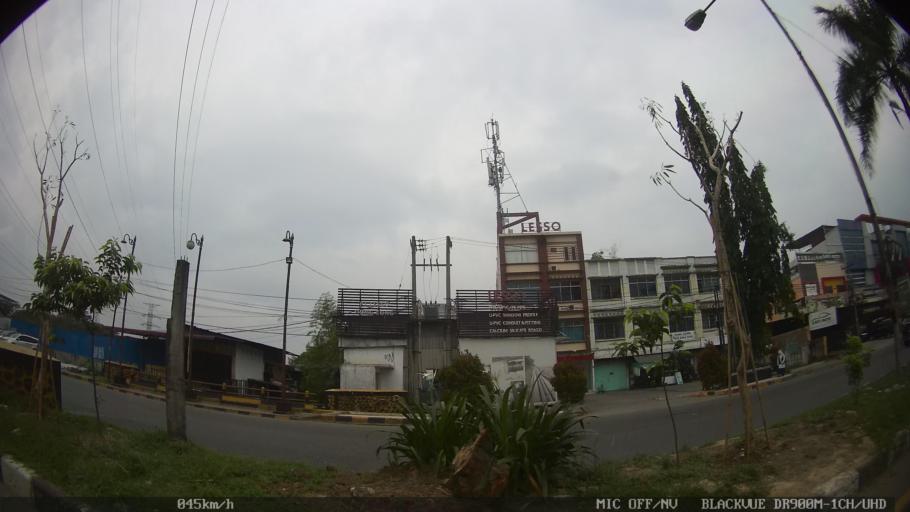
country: ID
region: North Sumatra
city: Deli Tua
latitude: 3.5376
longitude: 98.6930
